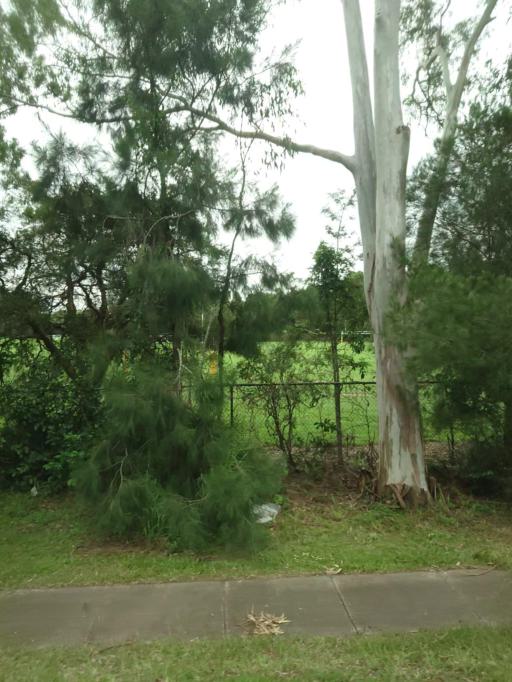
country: AU
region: Queensland
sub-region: Brisbane
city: Wynnum West
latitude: -27.4759
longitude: 153.1399
